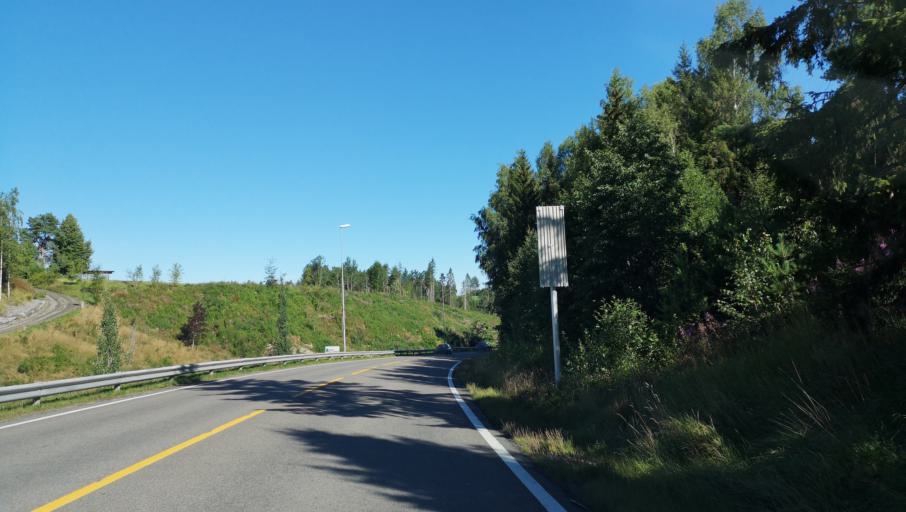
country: NO
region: Ostfold
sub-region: Spydeberg
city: Spydeberg
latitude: 59.5976
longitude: 11.1041
